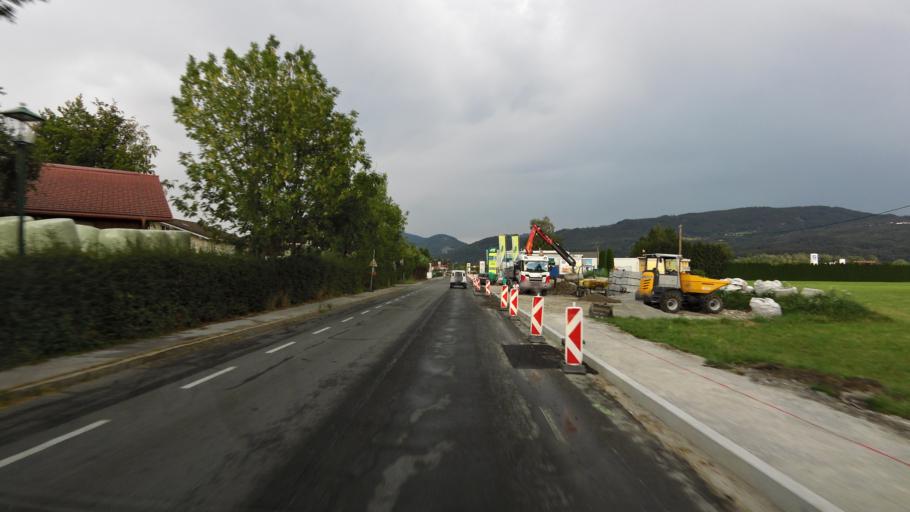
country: AT
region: Salzburg
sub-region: Politischer Bezirk Salzburg-Umgebung
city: Anif
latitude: 47.7307
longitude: 13.0631
